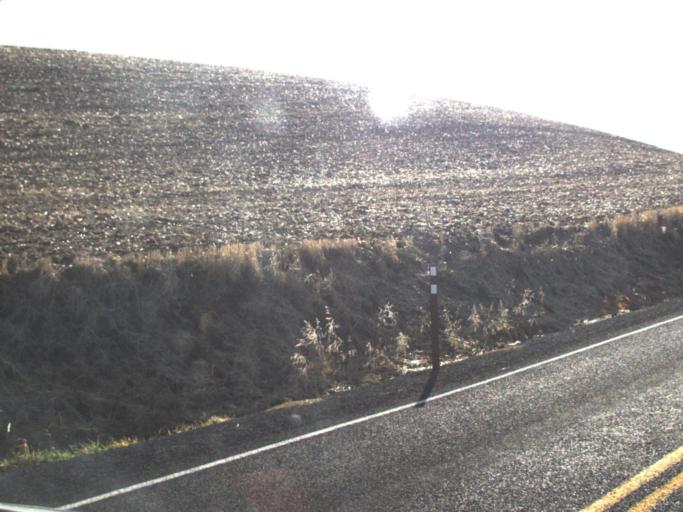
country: US
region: Washington
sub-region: Whitman County
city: Colfax
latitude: 46.9088
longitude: -117.2830
